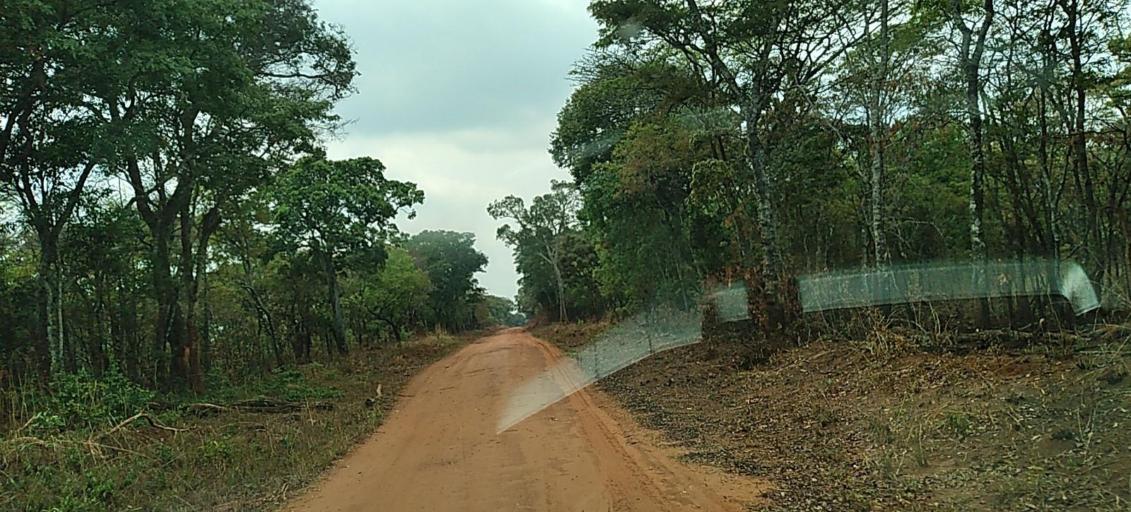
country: ZM
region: North-Western
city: Mwinilunga
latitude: -11.5509
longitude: 24.7742
